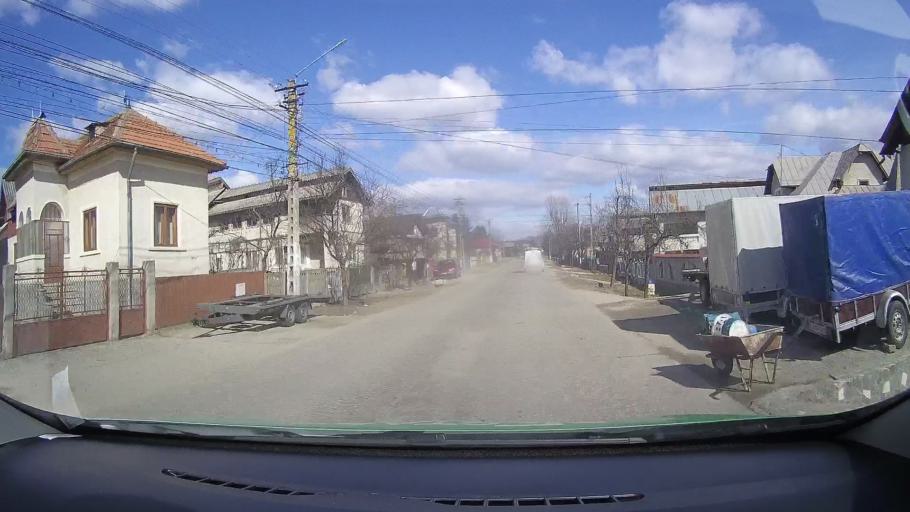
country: RO
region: Dambovita
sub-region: Comuna Branesti
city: Branesti
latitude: 45.0299
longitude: 25.4103
